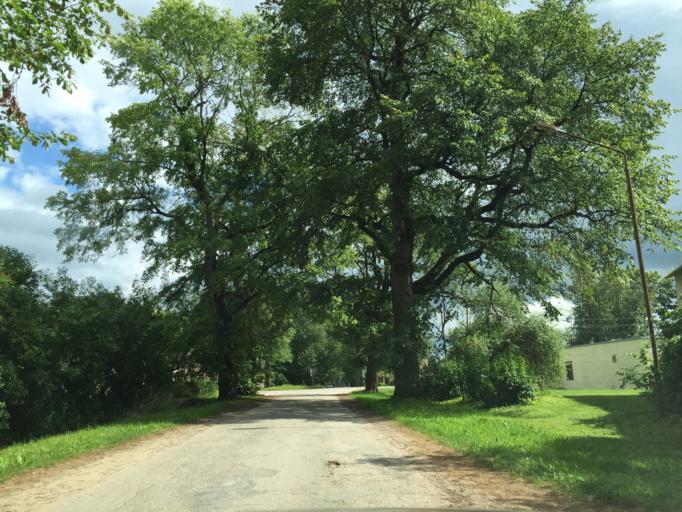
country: LV
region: Malpils
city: Malpils
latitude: 56.8592
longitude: 25.0201
